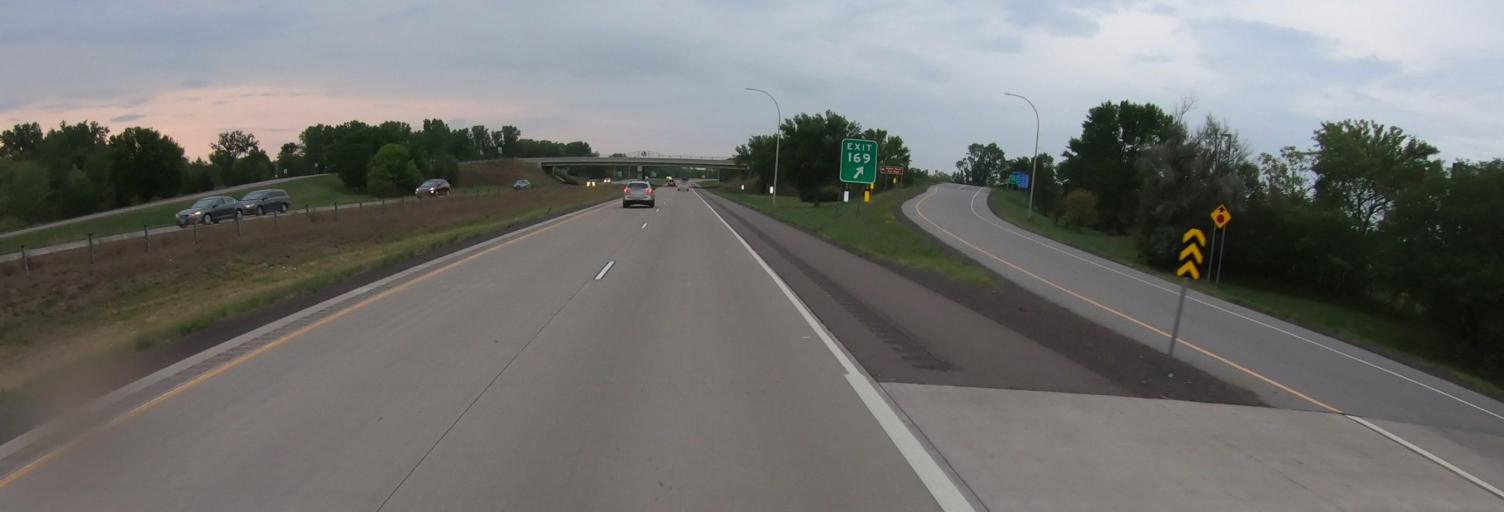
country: US
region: Minnesota
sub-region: Pine County
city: Pine City
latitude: 45.8202
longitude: -92.9833
